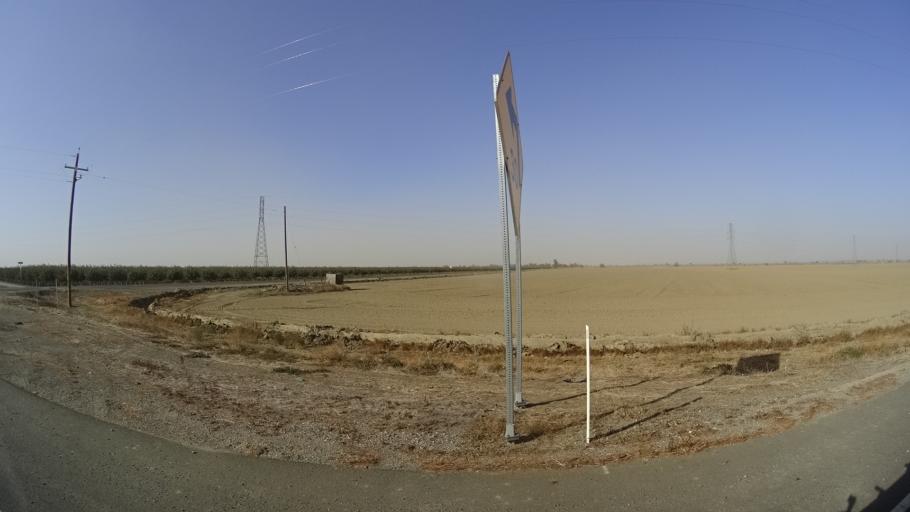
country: US
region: California
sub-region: Yolo County
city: Woodland
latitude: 38.7931
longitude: -121.7738
